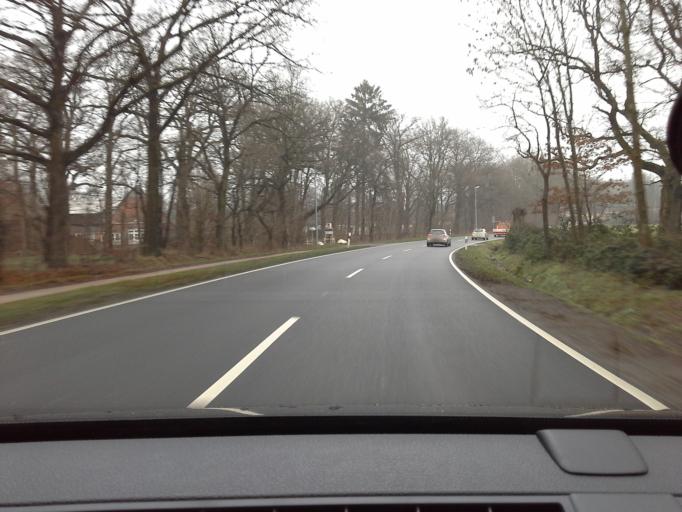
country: DE
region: Schleswig-Holstein
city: Ellerau
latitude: 53.7457
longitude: 9.9112
